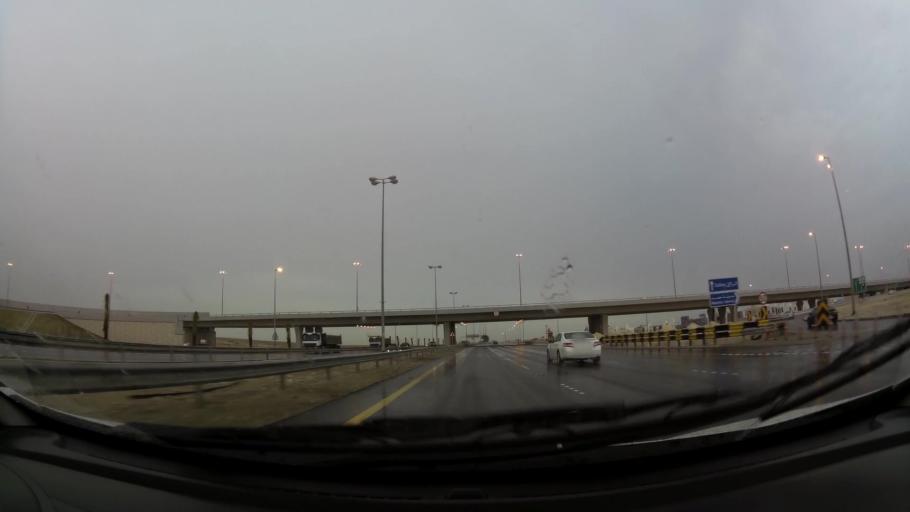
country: BH
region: Central Governorate
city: Dar Kulayb
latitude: 26.0825
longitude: 50.5152
